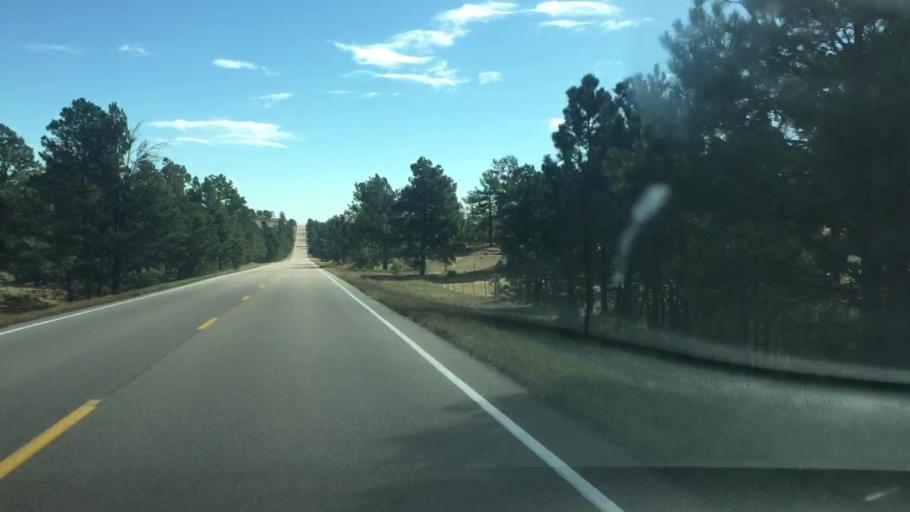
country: US
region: Colorado
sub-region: Elbert County
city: Kiowa
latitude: 39.2736
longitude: -104.1993
